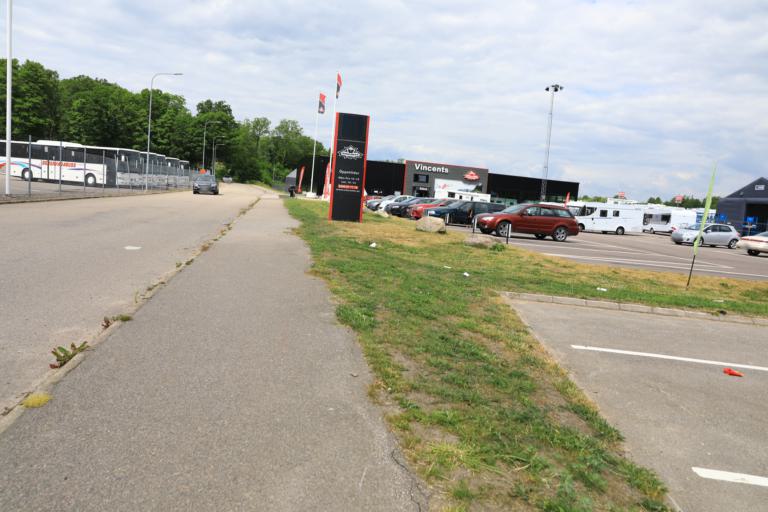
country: SE
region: Halland
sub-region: Varbergs Kommun
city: Varberg
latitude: 57.1694
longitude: 12.2762
